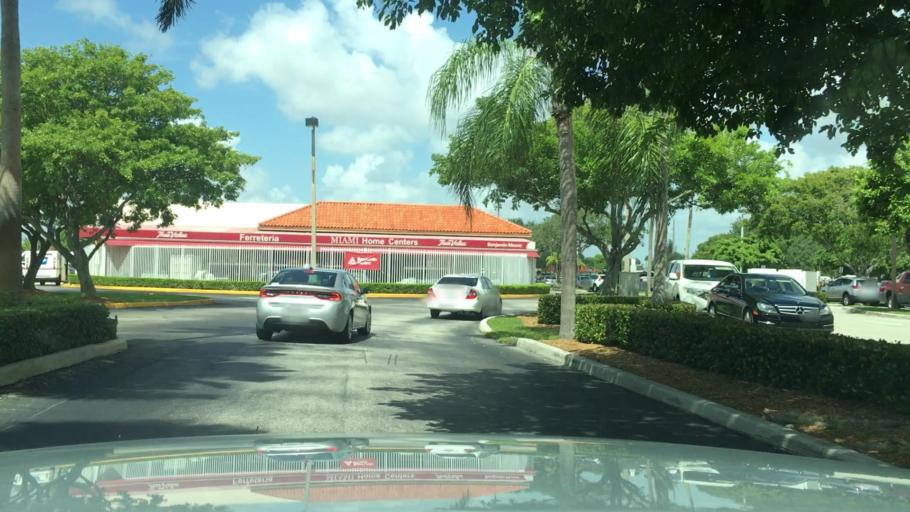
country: US
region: Florida
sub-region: Miami-Dade County
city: Tamiami
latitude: 25.7597
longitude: -80.4171
